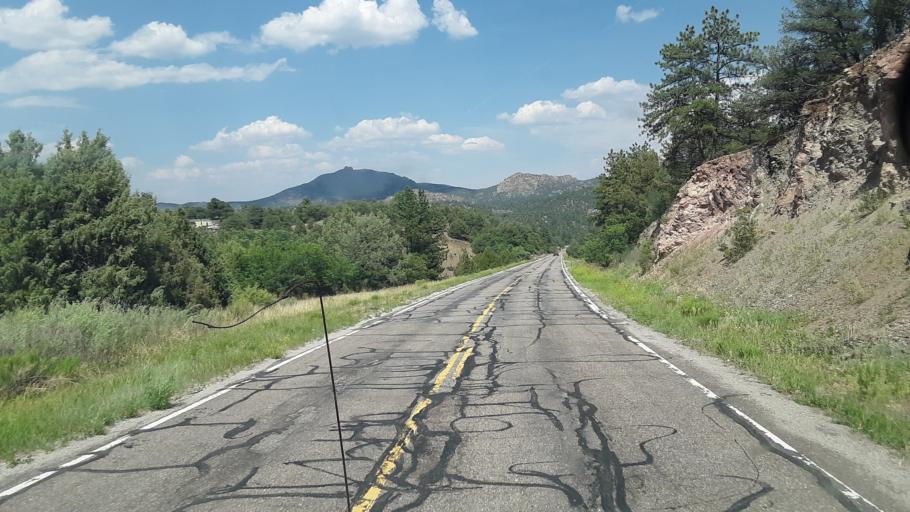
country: US
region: Colorado
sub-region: Custer County
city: Westcliffe
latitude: 38.3186
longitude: -105.6118
